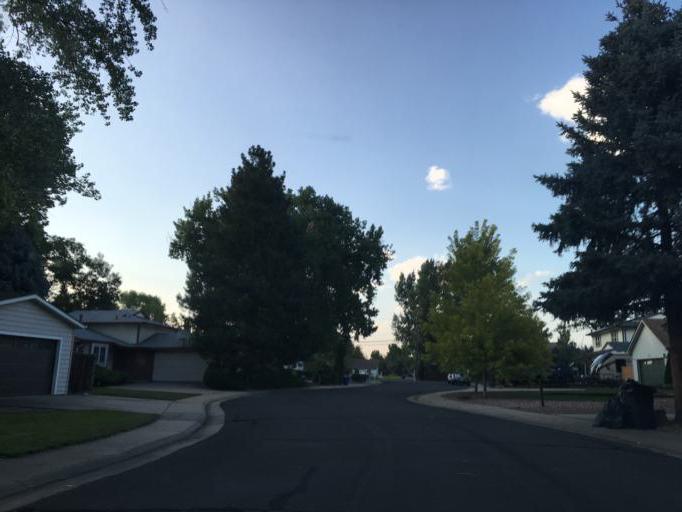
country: US
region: Colorado
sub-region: Jefferson County
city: Applewood
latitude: 39.7900
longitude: -105.1451
